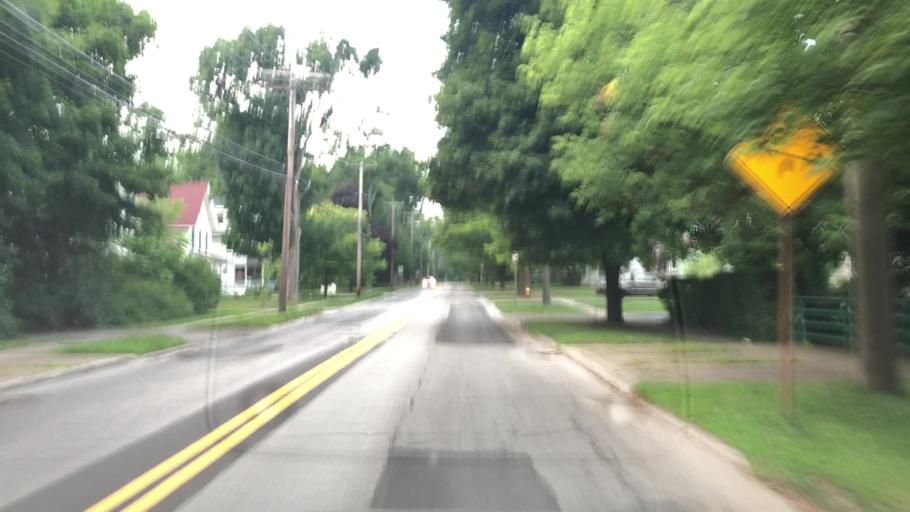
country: US
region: New York
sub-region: Erie County
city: East Aurora
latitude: 42.7696
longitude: -78.6078
